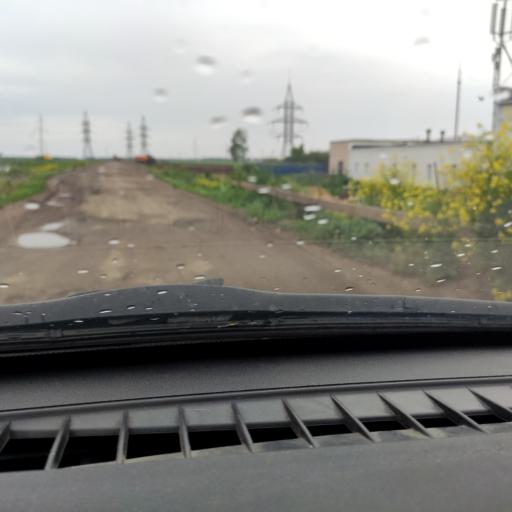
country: RU
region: Samara
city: Tol'yatti
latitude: 53.5922
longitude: 49.4390
